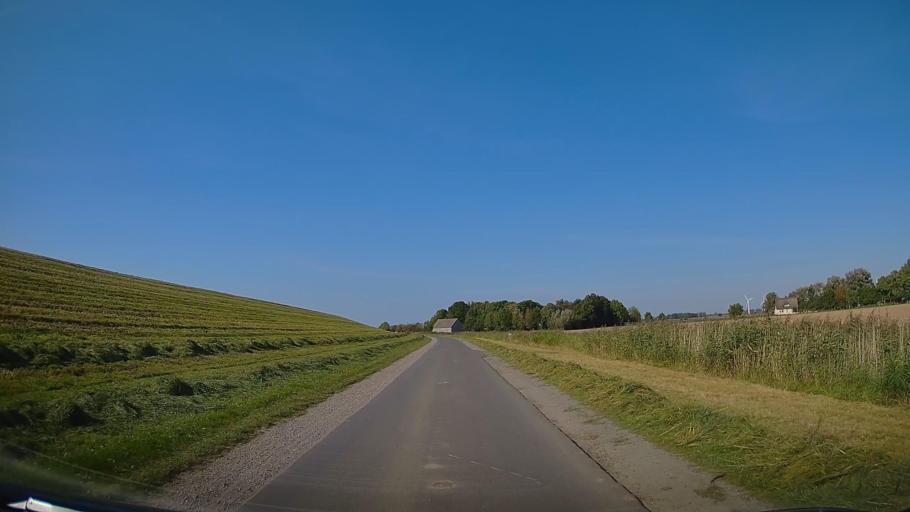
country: DE
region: Lower Saxony
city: Wremen
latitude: 53.6557
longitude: 8.4930
